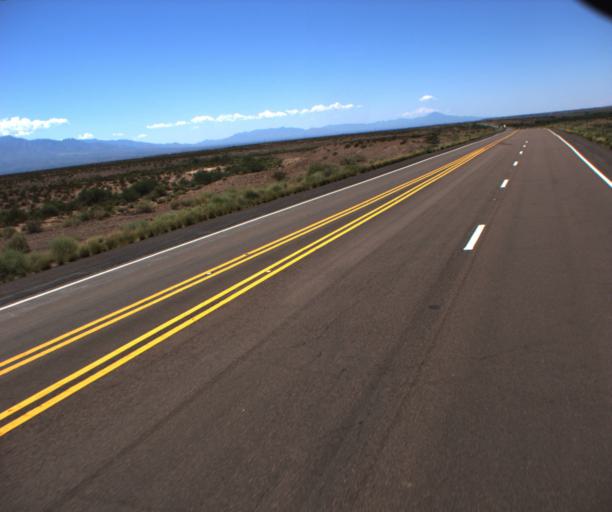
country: US
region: Arizona
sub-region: Graham County
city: Safford
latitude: 32.7937
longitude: -109.5536
